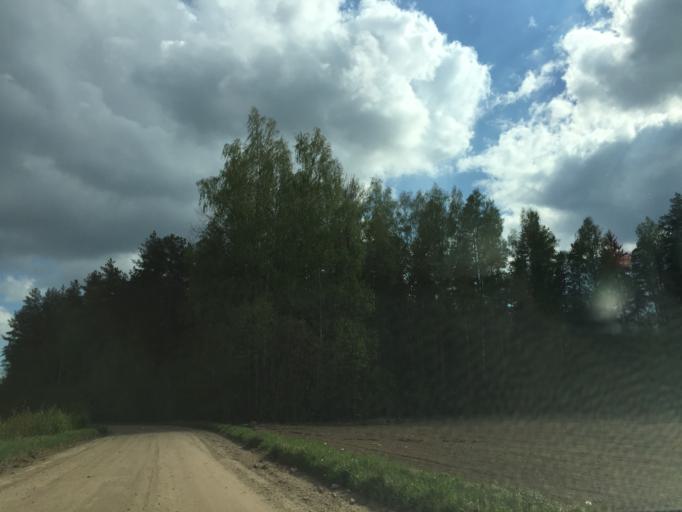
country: LV
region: Pargaujas
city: Stalbe
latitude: 57.3163
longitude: 24.8772
